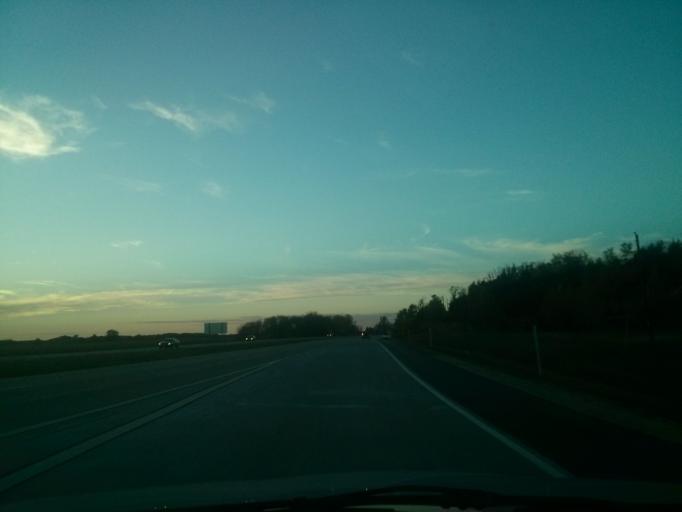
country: US
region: Wisconsin
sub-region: Pierce County
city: River Falls
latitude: 44.9004
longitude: -92.6516
